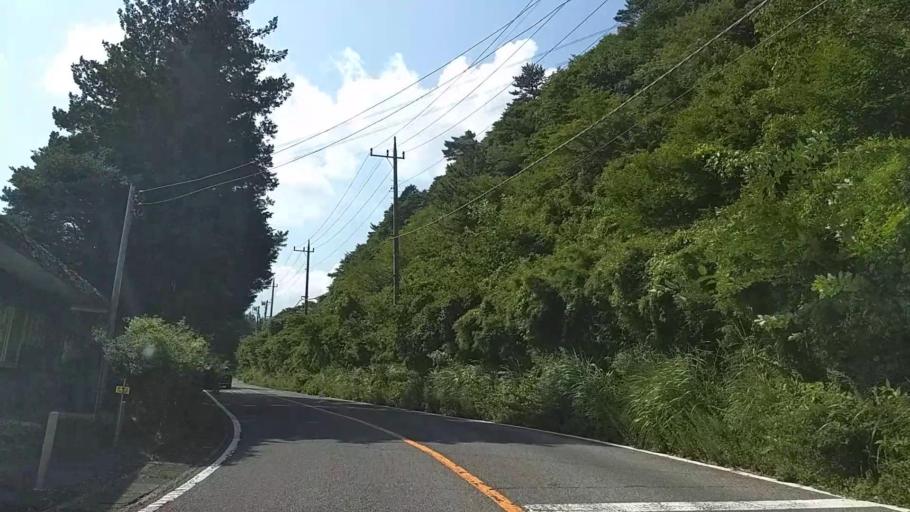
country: JP
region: Kanagawa
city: Hakone
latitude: 35.2150
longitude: 139.0150
